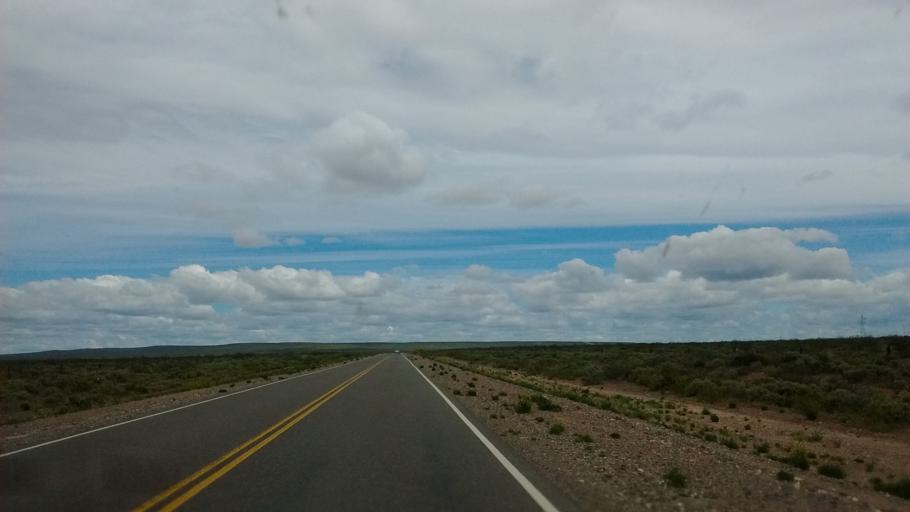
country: AR
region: Neuquen
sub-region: Departamento de Picun Leufu
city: Picun Leufu
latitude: -39.7073
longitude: -69.5062
